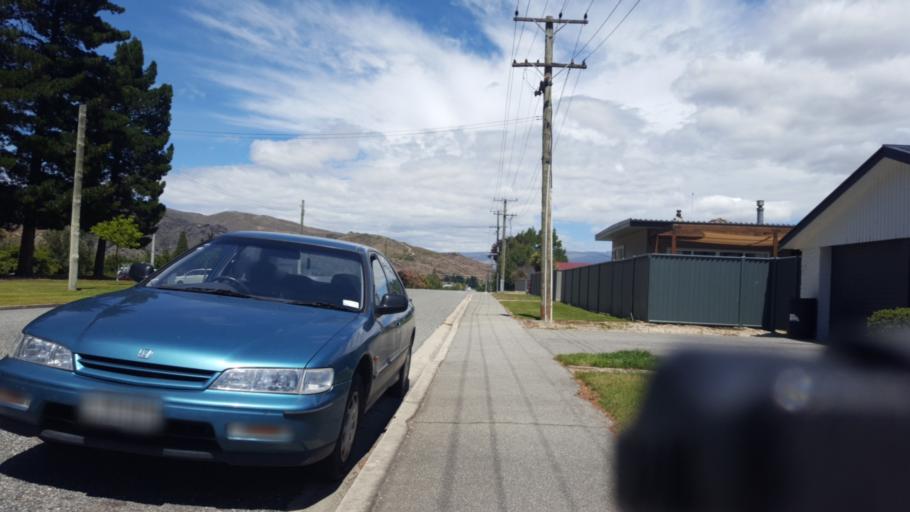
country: NZ
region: Otago
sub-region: Queenstown-Lakes District
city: Wanaka
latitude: -45.0424
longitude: 169.2077
